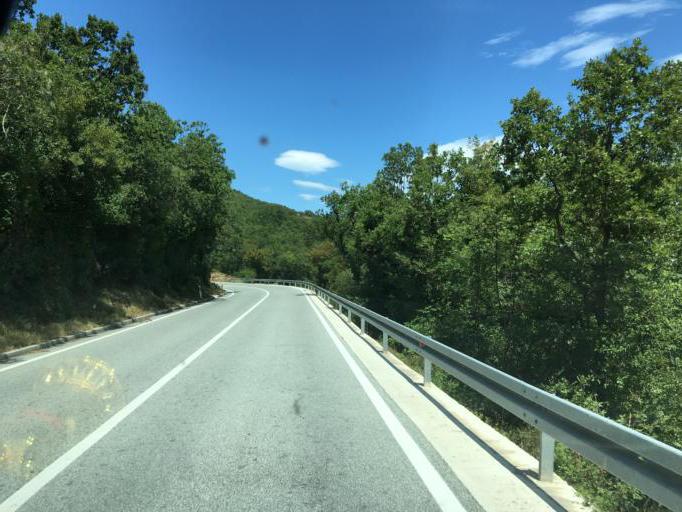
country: HR
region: Istarska
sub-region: Grad Labin
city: Rabac
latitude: 45.1350
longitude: 14.2059
